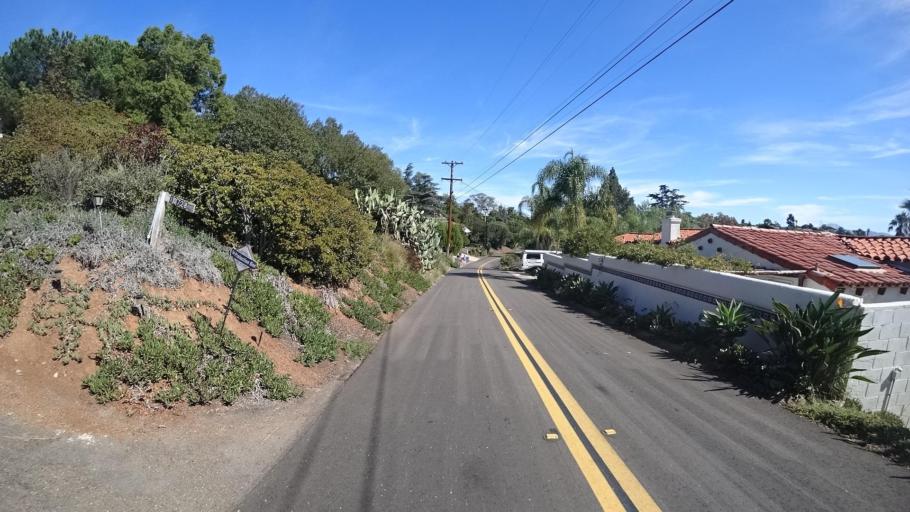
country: US
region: California
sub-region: San Diego County
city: Casa de Oro-Mount Helix
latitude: 32.7615
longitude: -116.9641
